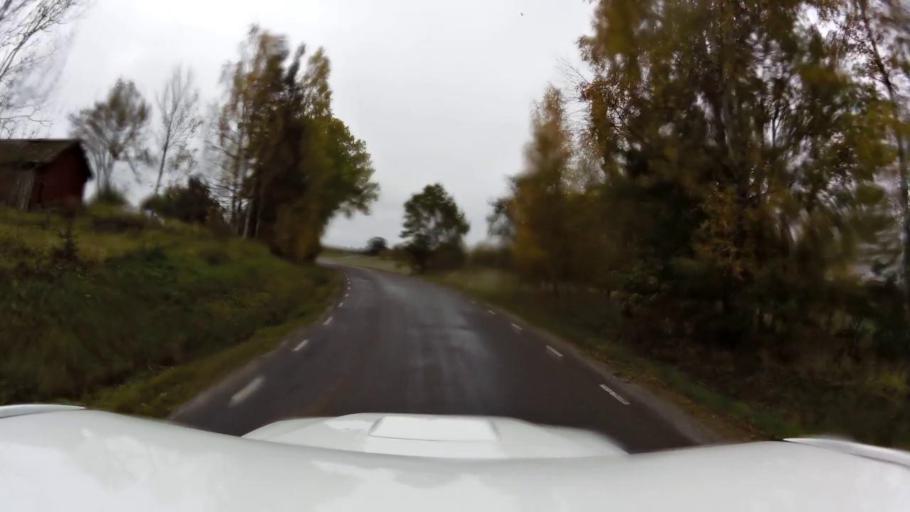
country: SE
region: OEstergoetland
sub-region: Linkopings Kommun
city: Linghem
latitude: 58.4748
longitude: 15.7226
